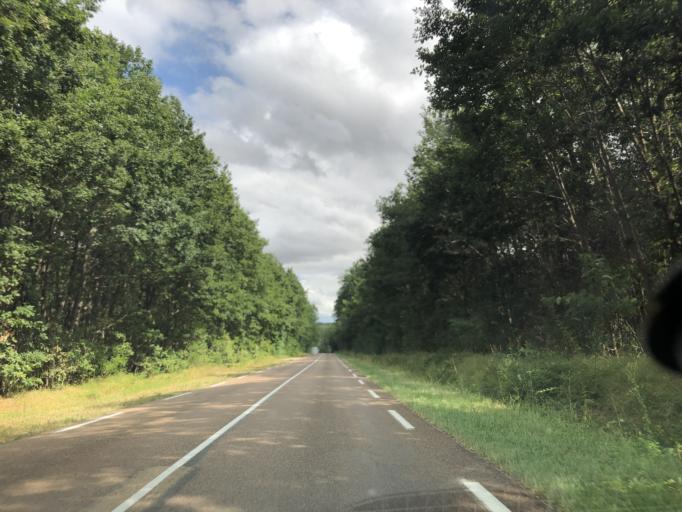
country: FR
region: Bourgogne
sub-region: Departement de l'Yonne
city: Charbuy
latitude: 47.8119
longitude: 3.4829
